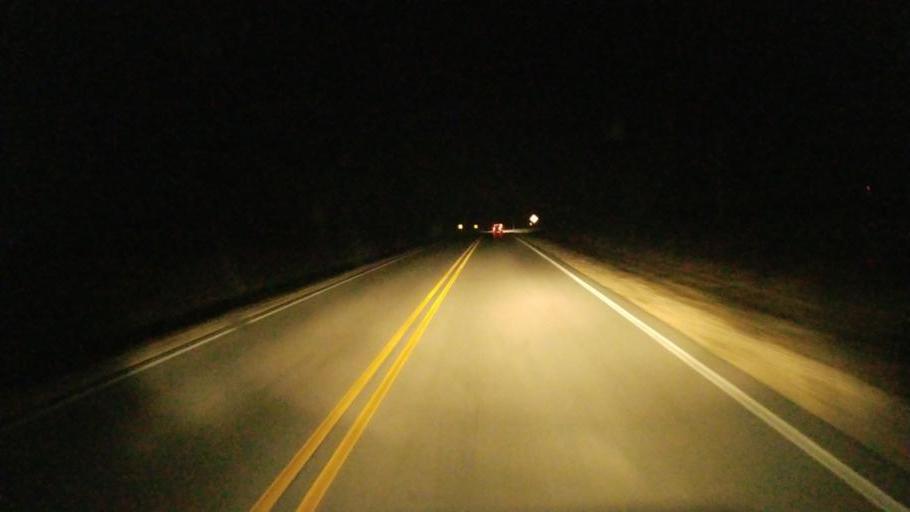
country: US
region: Illinois
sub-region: Henderson County
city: Oquawka
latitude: 40.7724
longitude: -90.8728
